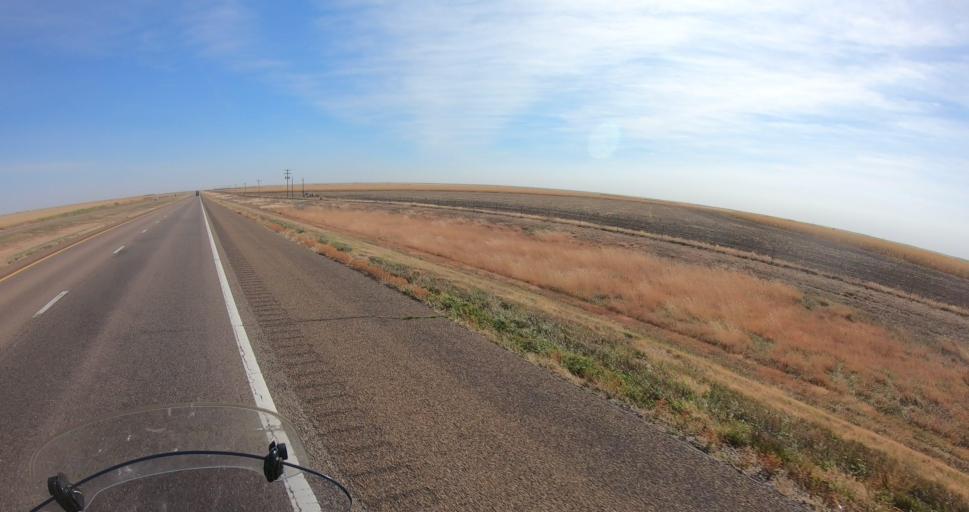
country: US
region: Kansas
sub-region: Sherman County
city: Goodland
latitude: 39.3300
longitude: -101.4589
